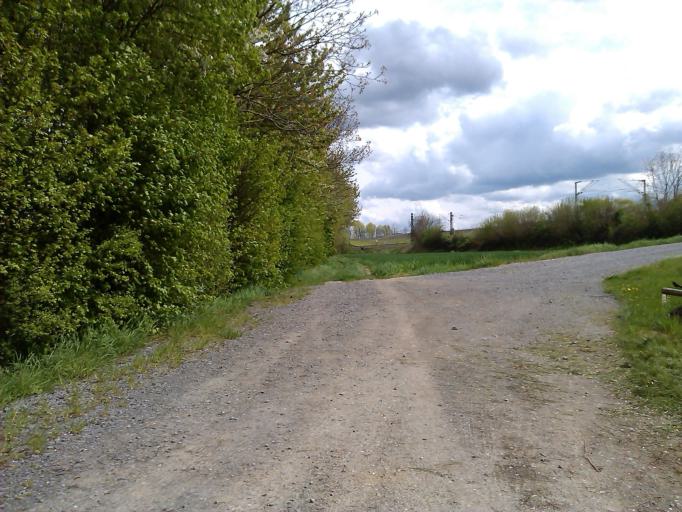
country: DE
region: Baden-Wuerttemberg
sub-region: Regierungsbezirk Stuttgart
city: Lauffen am Neckar
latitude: 49.0952
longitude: 9.1556
